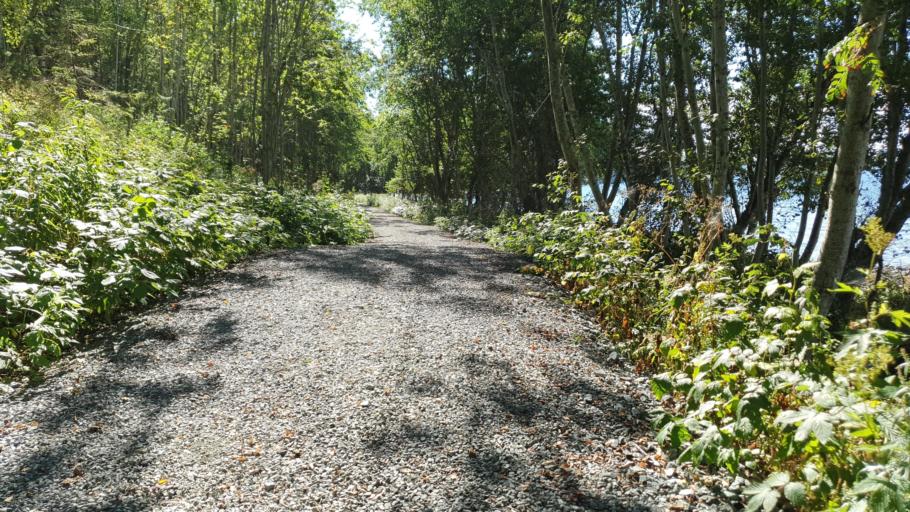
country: NO
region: Nord-Trondelag
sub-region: Levanger
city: Levanger
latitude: 63.7770
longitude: 11.3800
